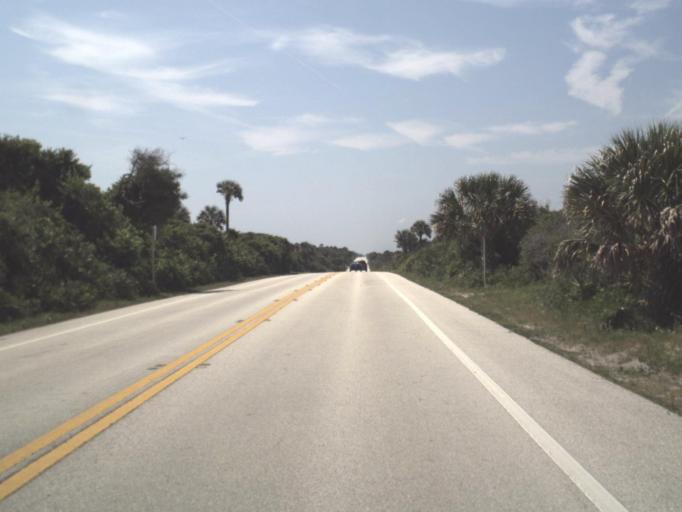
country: US
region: Florida
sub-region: Saint Johns County
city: Palm Valley
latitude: 30.1238
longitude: -81.3476
